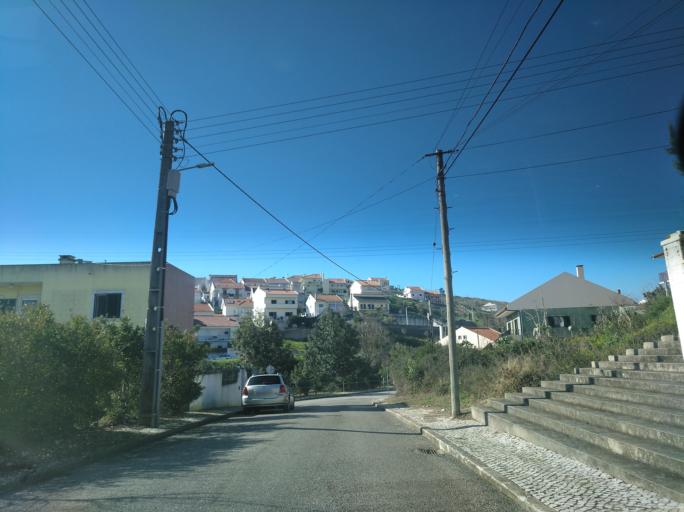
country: PT
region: Lisbon
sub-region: Odivelas
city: Famoes
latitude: 38.7920
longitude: -9.2205
